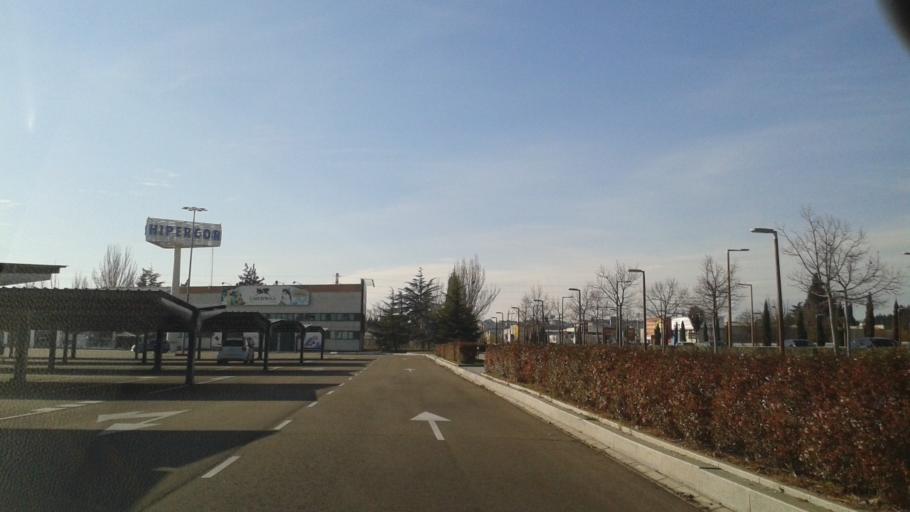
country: ES
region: Castille and Leon
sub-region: Provincia de Valladolid
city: Arroyo
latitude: 41.6234
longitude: -4.7698
